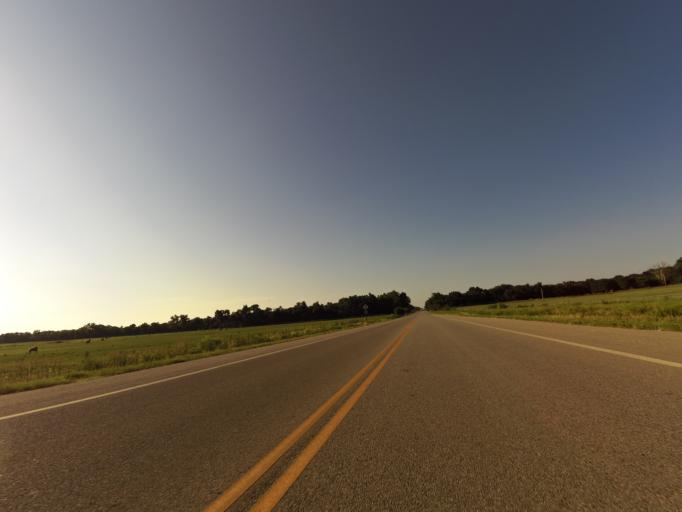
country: US
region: Kansas
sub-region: Reno County
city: Buhler
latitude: 38.1557
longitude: -97.8487
